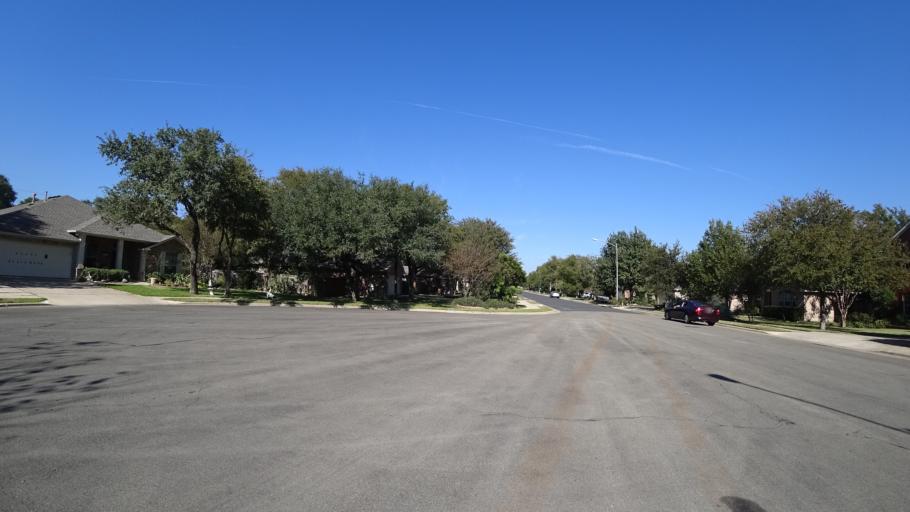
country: US
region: Texas
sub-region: Travis County
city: Shady Hollow
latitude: 30.1946
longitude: -97.8550
